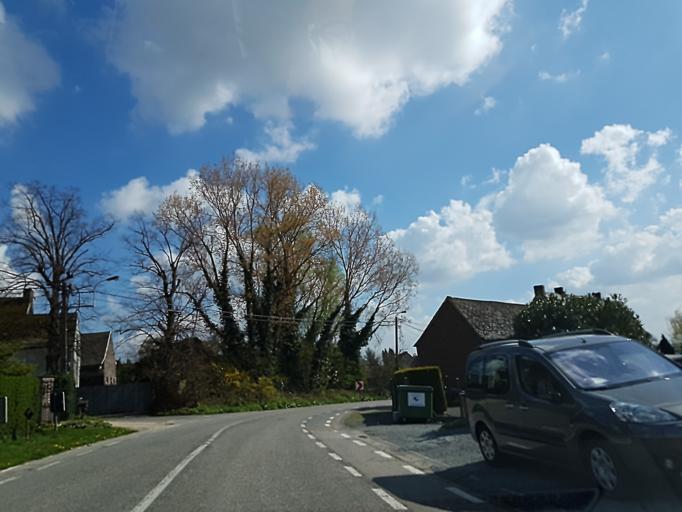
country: BE
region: Flanders
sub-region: Provincie Oost-Vlaanderen
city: Sint-Maria-Lierde
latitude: 50.8249
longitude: 3.8801
